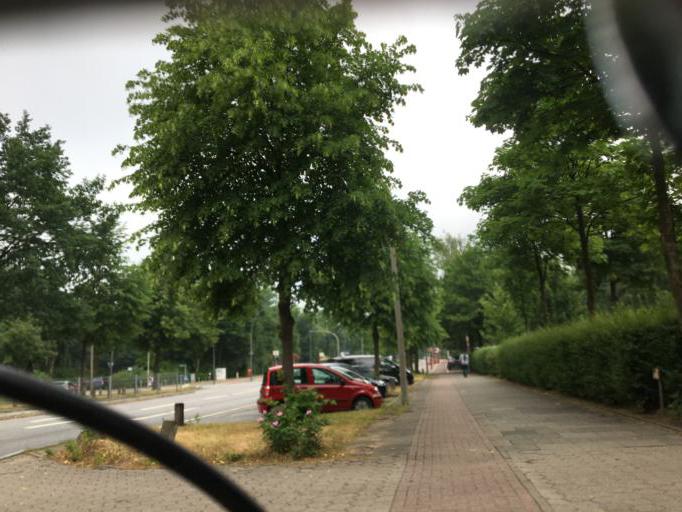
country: DE
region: Schleswig-Holstein
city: Halstenbek
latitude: 53.5916
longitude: 9.8528
